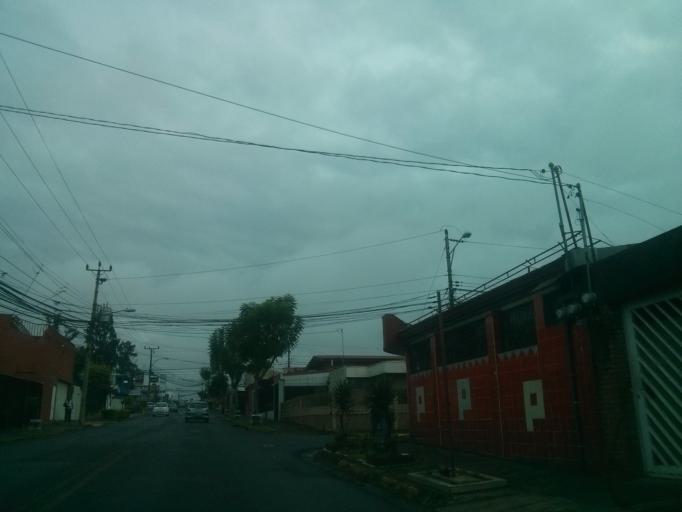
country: CR
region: San Jose
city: San Pedro
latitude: 9.9196
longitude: -84.0432
